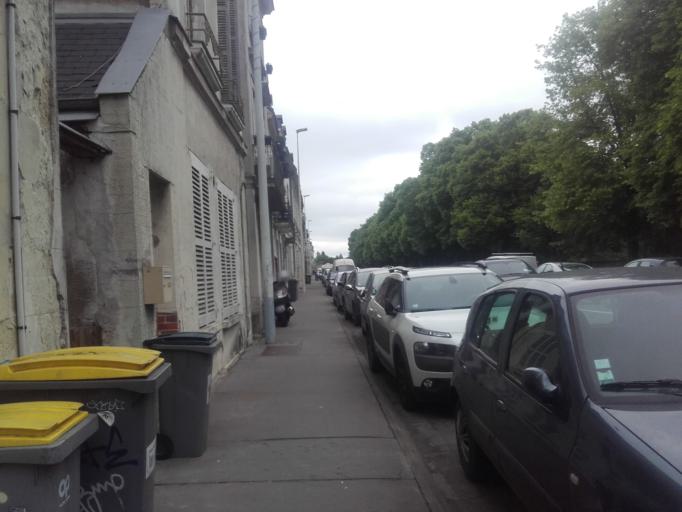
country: FR
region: Centre
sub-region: Departement d'Indre-et-Loire
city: Tours
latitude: 47.4018
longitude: 0.6898
